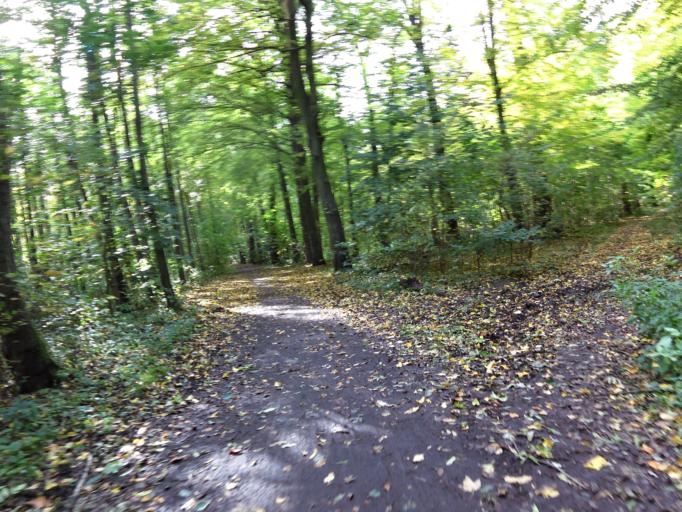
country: DE
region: Saxony
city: Markkleeberg
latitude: 51.3056
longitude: 12.3570
